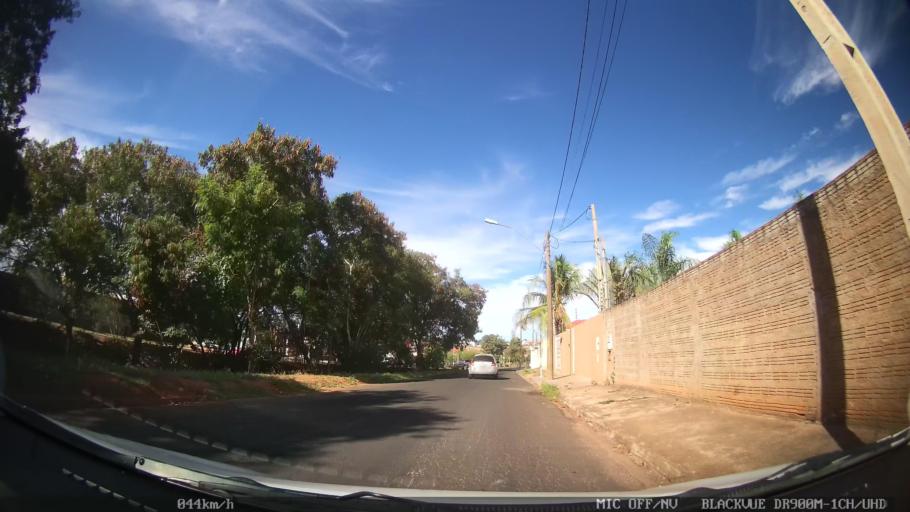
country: BR
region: Sao Paulo
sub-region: Catanduva
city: Catanduva
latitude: -21.1253
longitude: -48.9606
